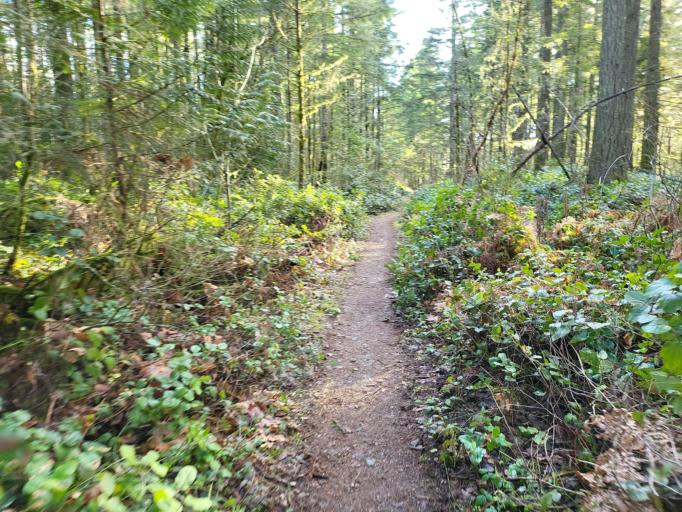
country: US
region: Washington
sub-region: King County
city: Issaquah
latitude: 47.5225
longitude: -122.0210
